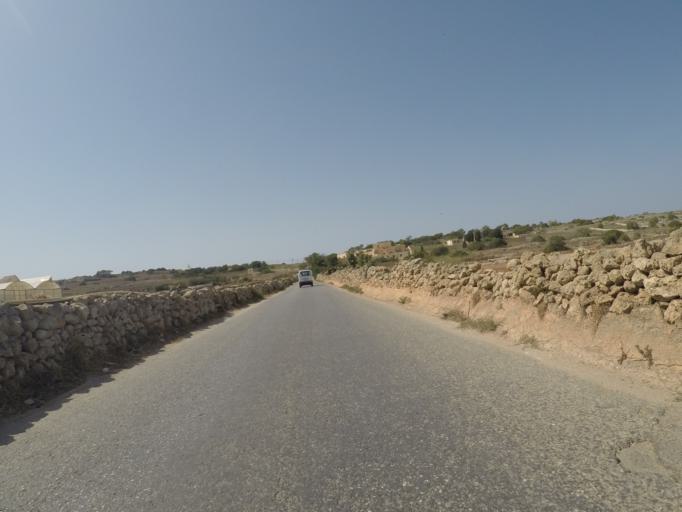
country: MT
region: L-Imgarr
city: Imgarr
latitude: 35.9252
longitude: 14.3788
